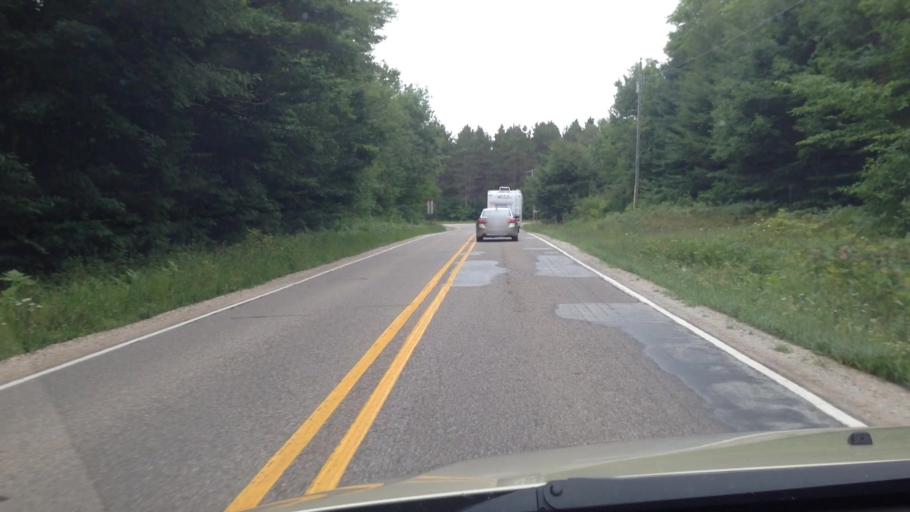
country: US
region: Michigan
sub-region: Mackinac County
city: Saint Ignace
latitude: 46.0554
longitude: -85.1508
